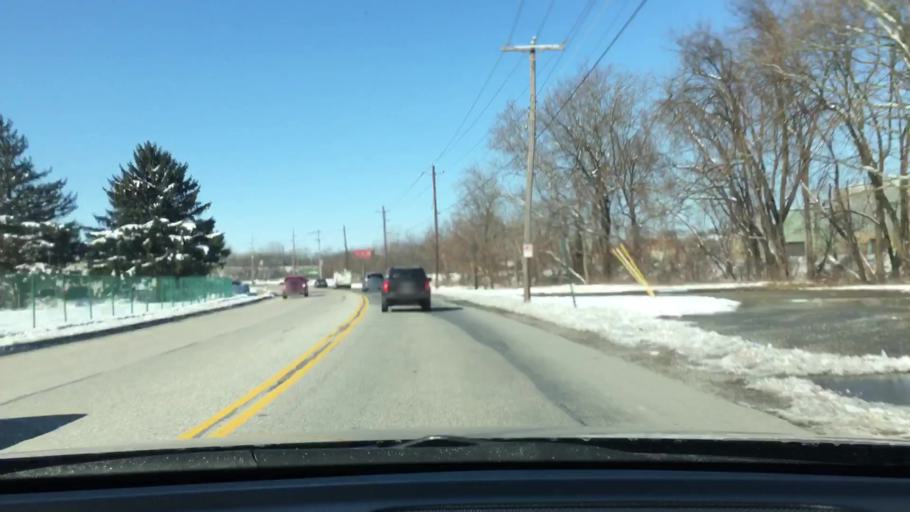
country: US
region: Pennsylvania
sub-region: York County
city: East York
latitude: 39.9780
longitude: -76.6904
